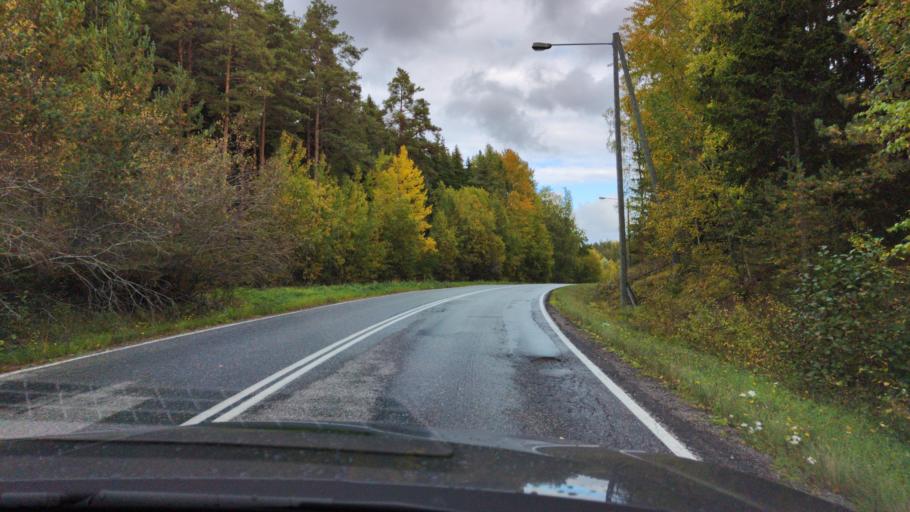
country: FI
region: Varsinais-Suomi
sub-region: Aboland-Turunmaa
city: Pargas
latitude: 60.3728
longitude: 22.2664
